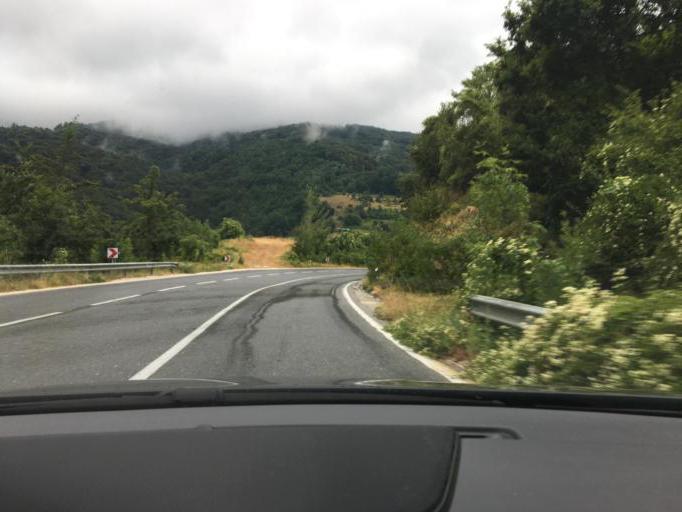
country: MK
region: Kriva Palanka
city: Kriva Palanka
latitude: 42.2185
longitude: 22.4385
